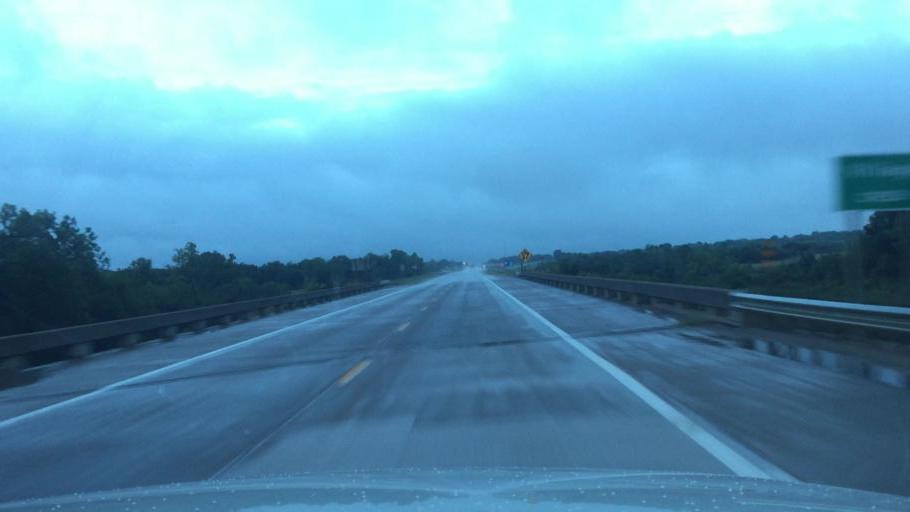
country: US
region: Kansas
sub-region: Neosho County
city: Chanute
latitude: 37.7006
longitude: -95.4794
